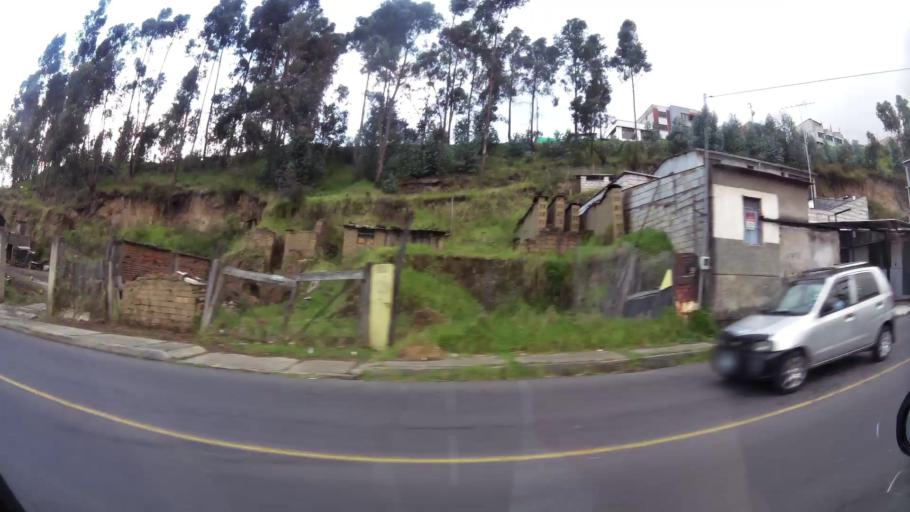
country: EC
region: Pichincha
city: Quito
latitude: -0.2791
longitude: -78.4950
